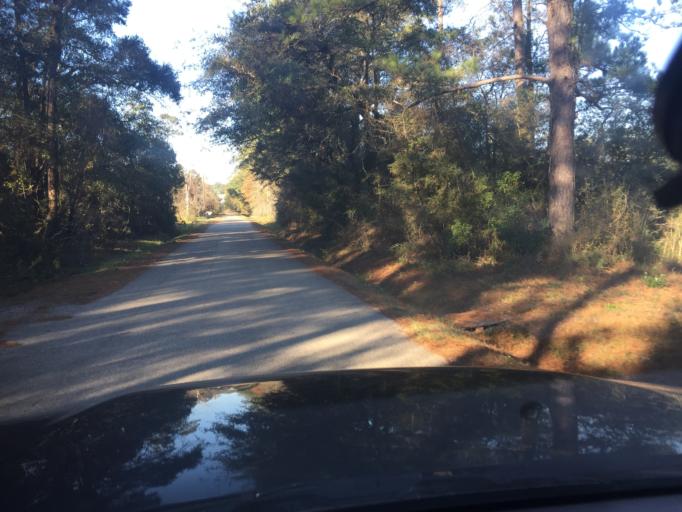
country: US
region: Louisiana
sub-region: Saint Tammany Parish
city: Slidell
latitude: 30.2439
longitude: -89.7672
